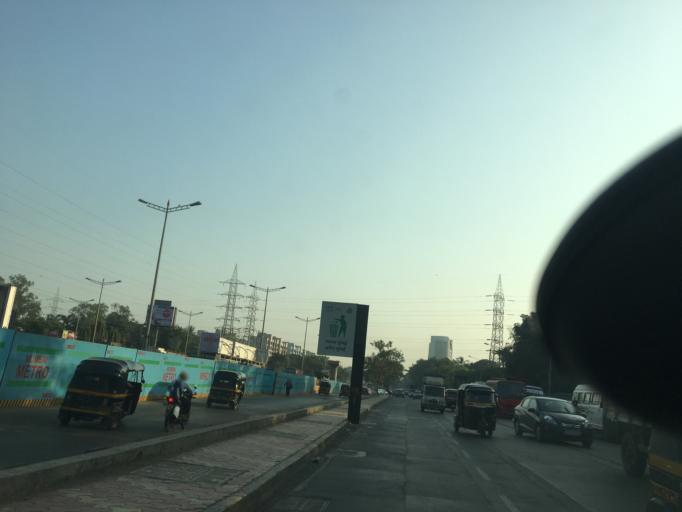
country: IN
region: Maharashtra
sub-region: Mumbai Suburban
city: Powai
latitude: 19.1520
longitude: 72.8563
